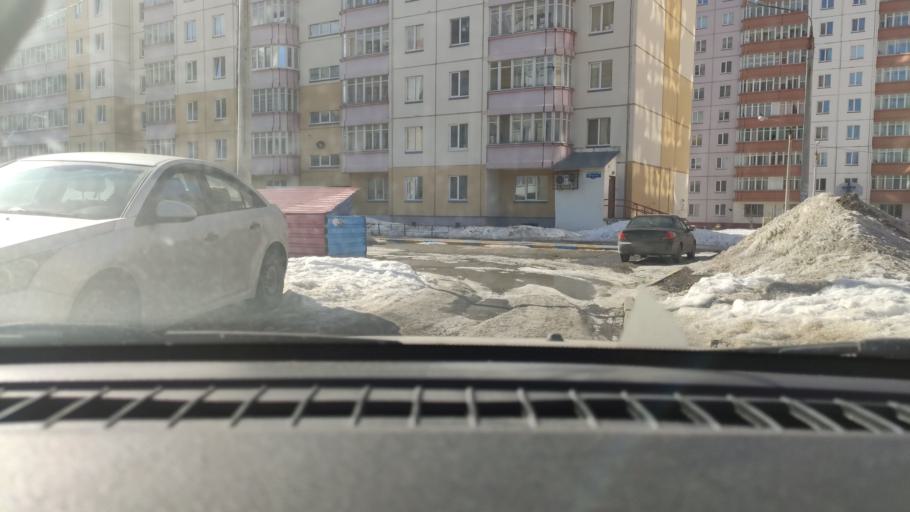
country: RU
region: Perm
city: Polazna
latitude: 58.1353
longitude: 56.4003
